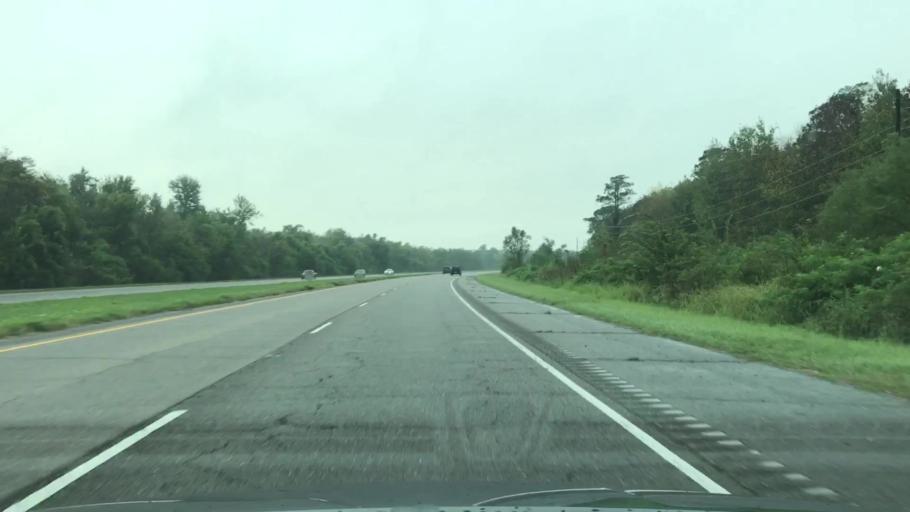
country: US
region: Louisiana
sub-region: Lafourche Parish
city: Raceland
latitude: 29.7235
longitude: -90.5599
